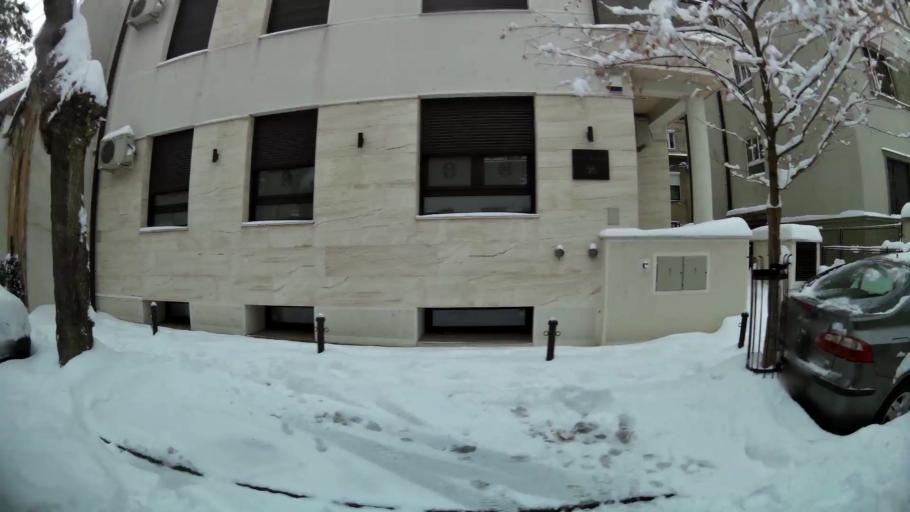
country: RS
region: Central Serbia
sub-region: Belgrade
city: Vracar
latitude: 44.7966
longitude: 20.4808
